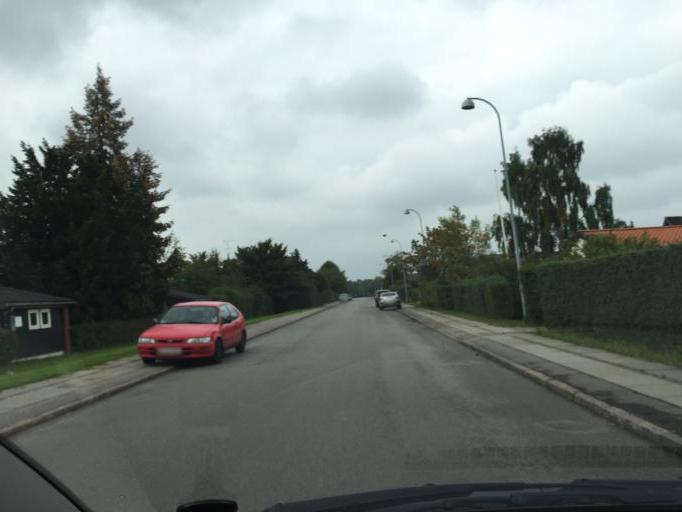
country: DK
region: Capital Region
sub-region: Herlev Kommune
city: Herlev
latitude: 55.7494
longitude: 12.4555
